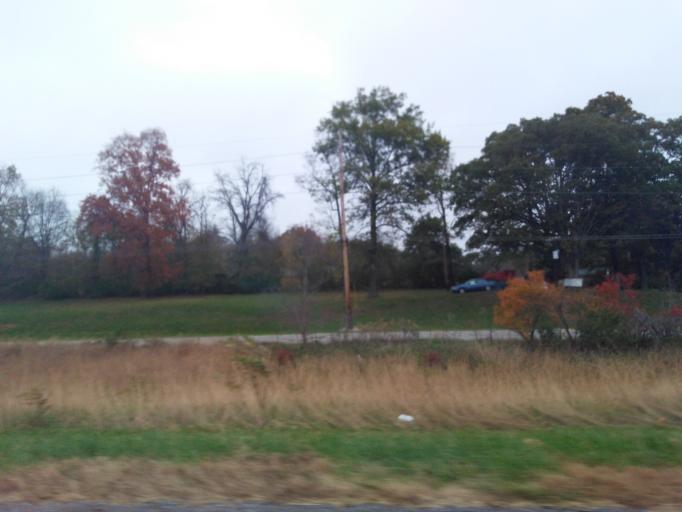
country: US
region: Illinois
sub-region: Bond County
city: Greenville
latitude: 38.8387
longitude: -89.5004
